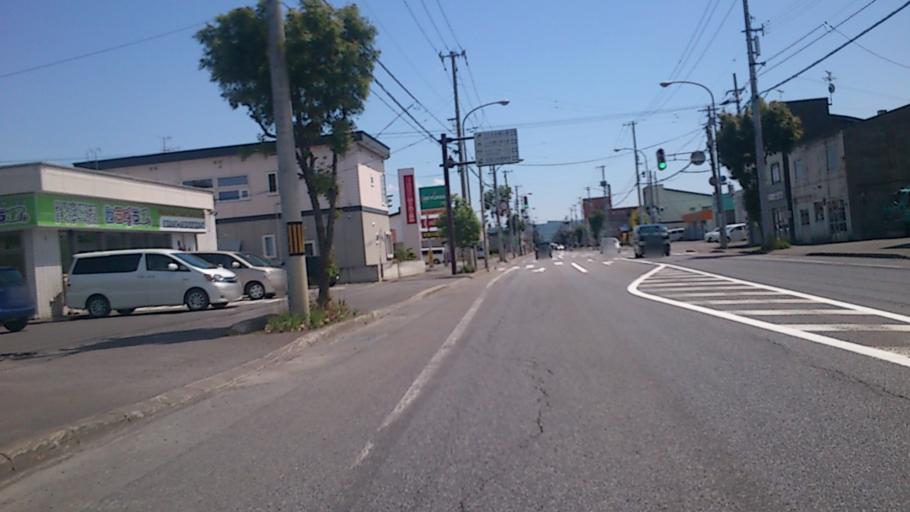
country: JP
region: Hokkaido
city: Nayoro
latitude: 44.1841
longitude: 142.3898
